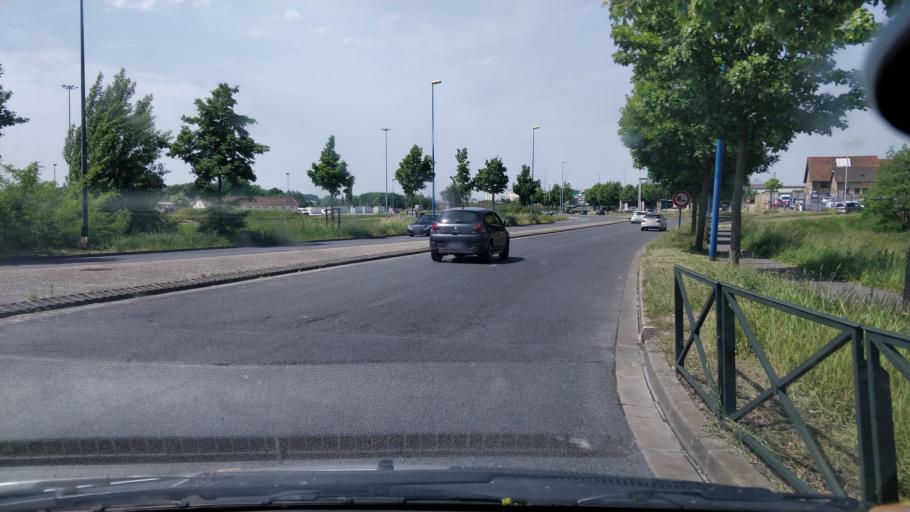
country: FR
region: Ile-de-France
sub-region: Departement de Seine-et-Marne
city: Chelles
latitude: 48.8771
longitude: 2.6080
